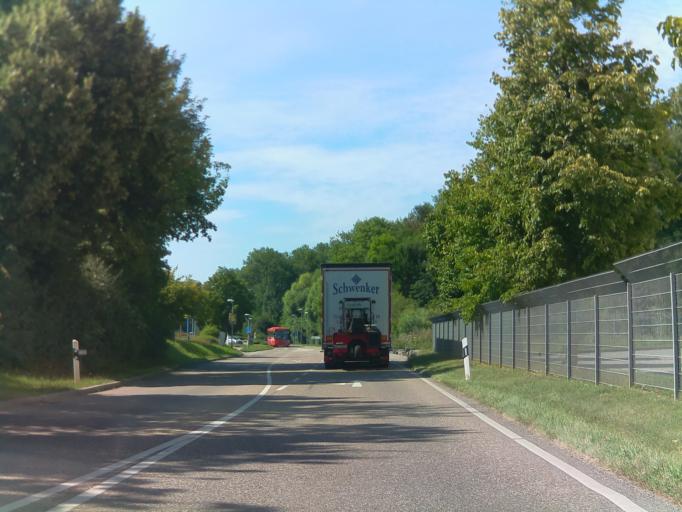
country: DE
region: Baden-Wuerttemberg
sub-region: Karlsruhe Region
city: Oberderdingen
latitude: 49.0727
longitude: 8.7946
